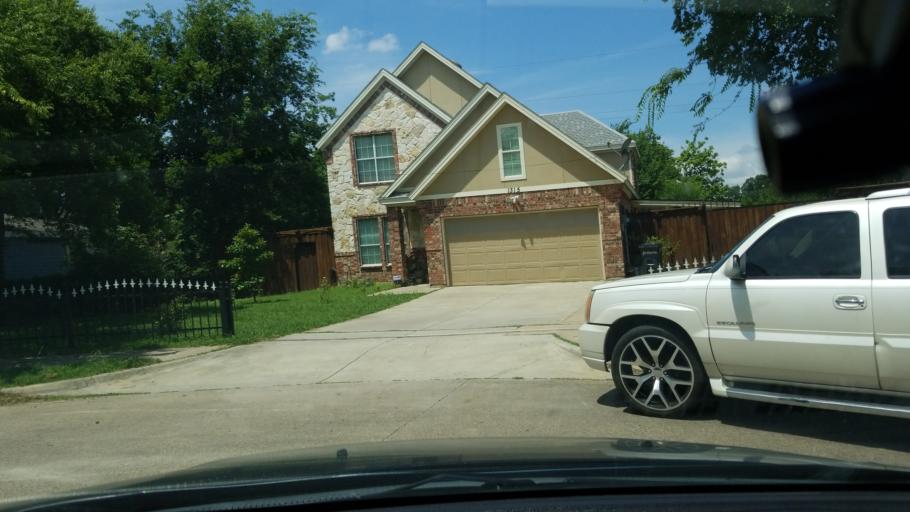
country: US
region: Texas
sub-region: Dallas County
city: Balch Springs
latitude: 32.7513
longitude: -96.6259
